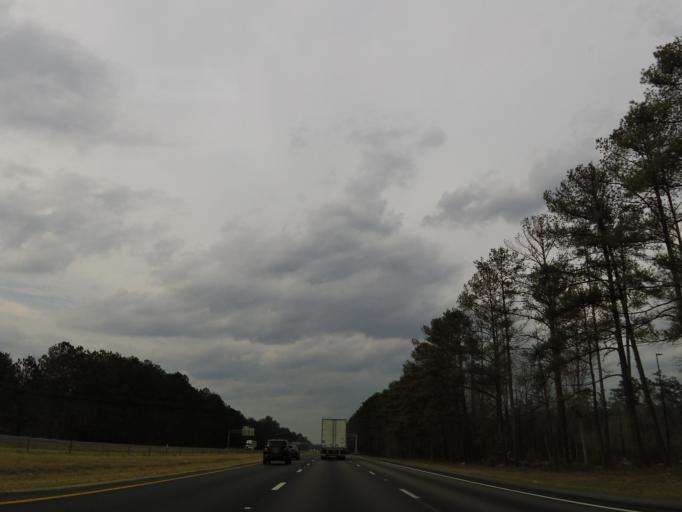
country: US
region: South Carolina
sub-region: Lexington County
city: Pineridge
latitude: 33.8952
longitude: -81.0442
